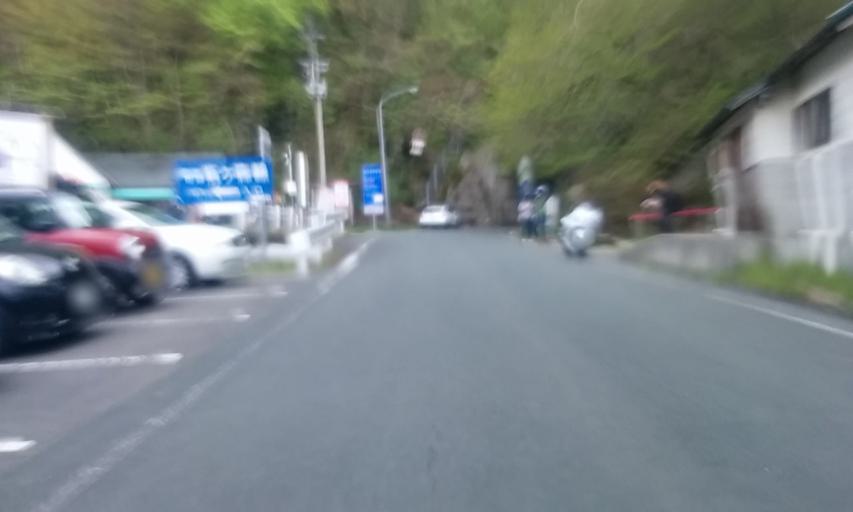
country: JP
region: Ehime
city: Saijo
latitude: 33.8001
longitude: 133.2666
